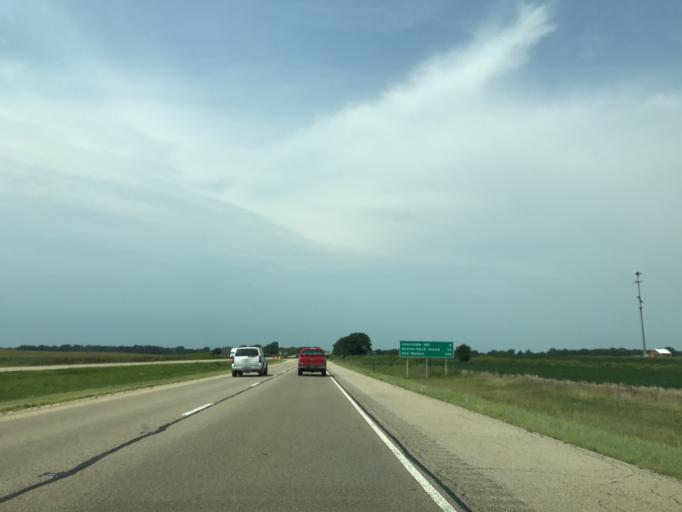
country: US
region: Illinois
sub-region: Bureau County
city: Ladd
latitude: 41.3704
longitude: -89.2342
